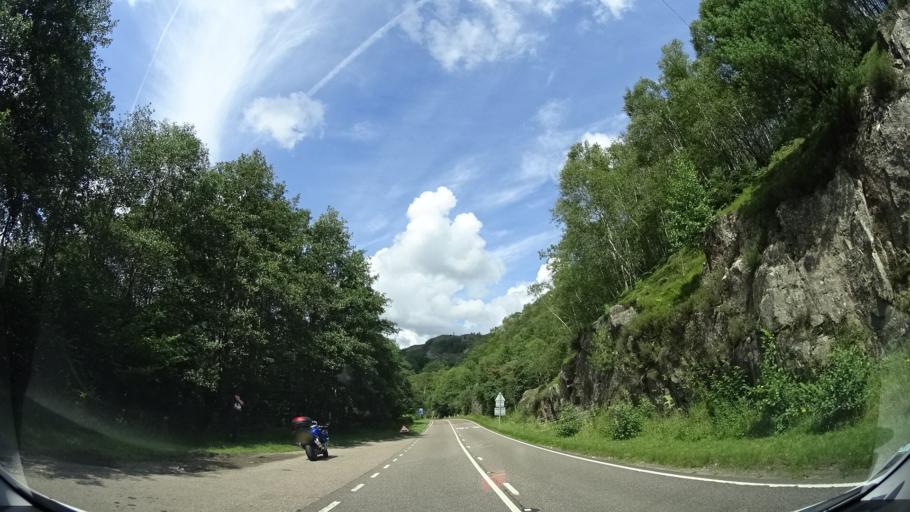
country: GB
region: Scotland
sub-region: Highland
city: Fort William
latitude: 56.8619
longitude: -5.4103
